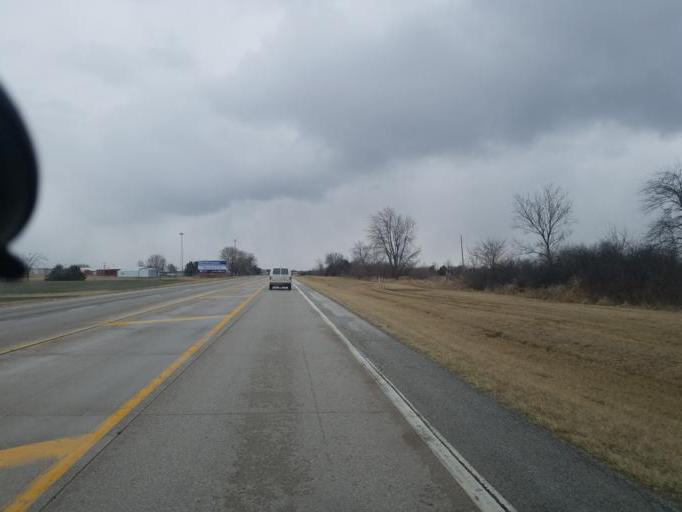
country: US
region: Missouri
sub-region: Macon County
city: Macon
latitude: 39.7713
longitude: -92.4732
